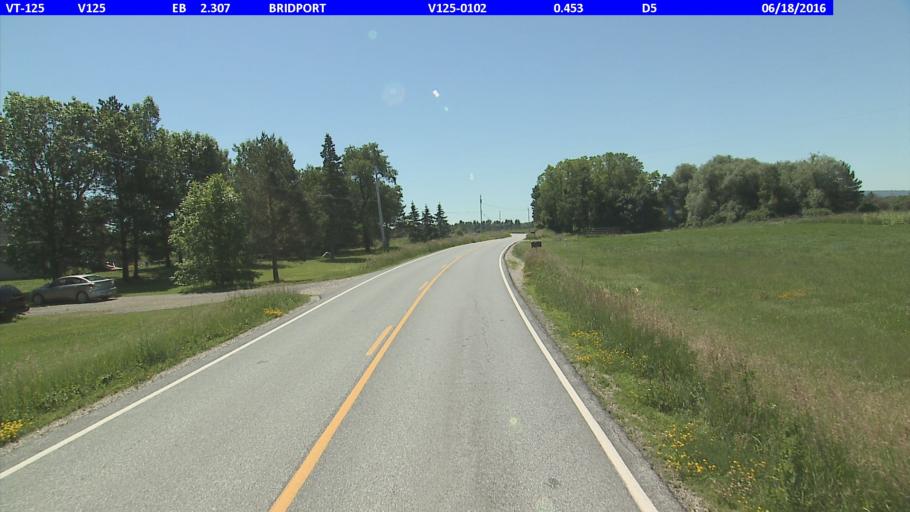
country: US
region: New York
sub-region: Essex County
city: Port Henry
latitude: 44.0156
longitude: -73.3893
